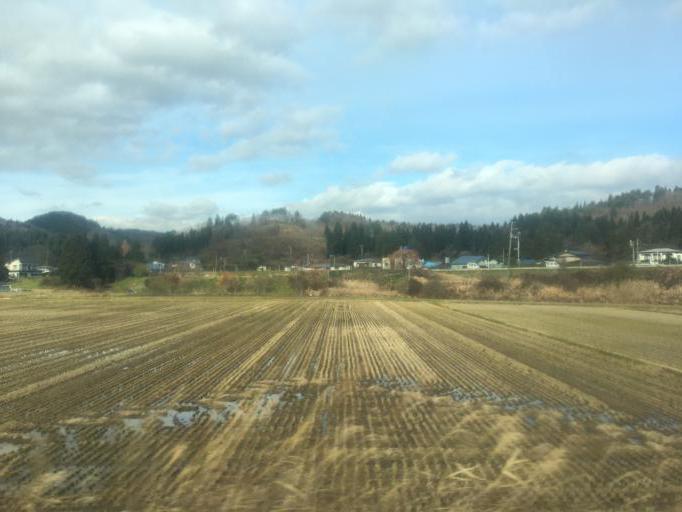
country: JP
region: Akita
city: Takanosu
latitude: 40.2196
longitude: 140.3228
